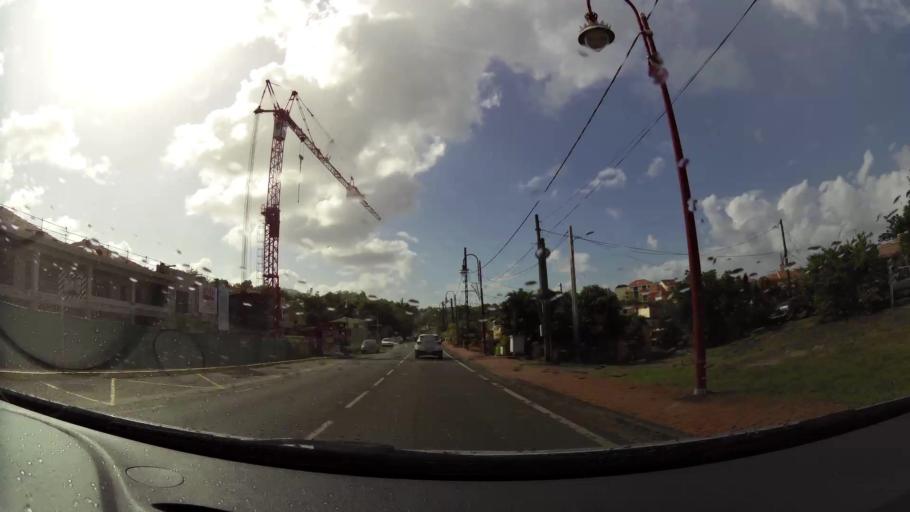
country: MQ
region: Martinique
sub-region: Martinique
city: Les Trois-Ilets
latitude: 14.5363
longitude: -61.0319
